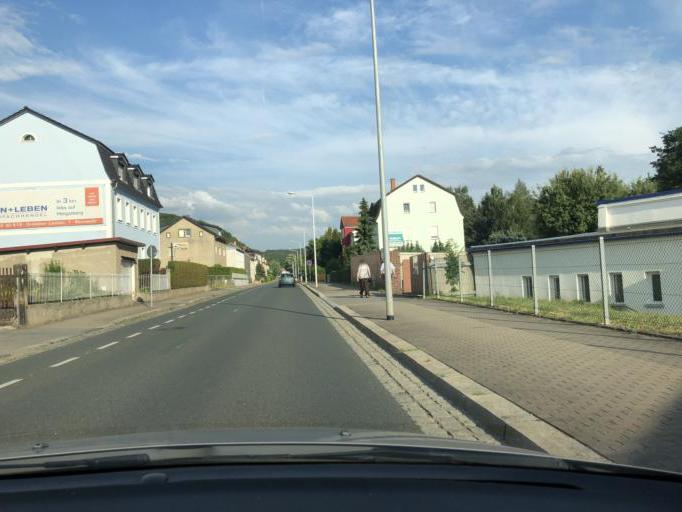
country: DE
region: Saxony
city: Freital
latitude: 50.9911
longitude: 13.6608
